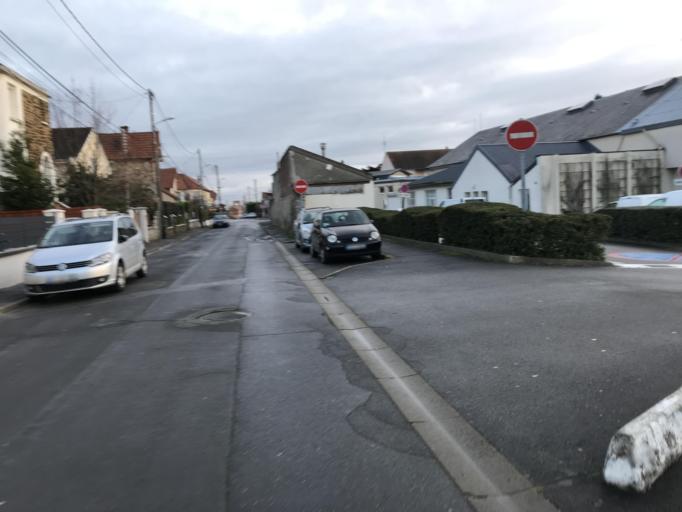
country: FR
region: Ile-de-France
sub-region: Departement de l'Essonne
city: Savigny-sur-Orge
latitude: 48.6802
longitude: 2.3458
